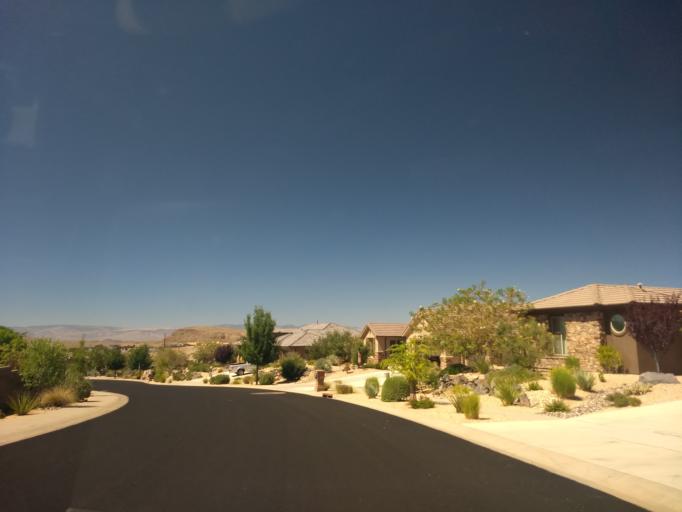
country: US
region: Utah
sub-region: Washington County
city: Washington
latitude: 37.1415
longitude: -113.4692
